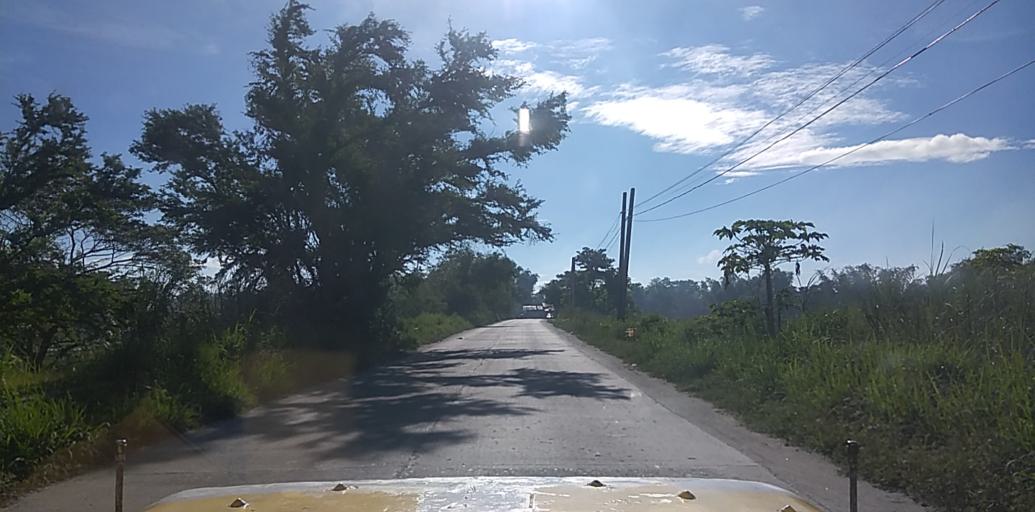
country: PH
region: Central Luzon
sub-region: Province of Pampanga
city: Anao
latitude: 15.1201
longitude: 120.7019
